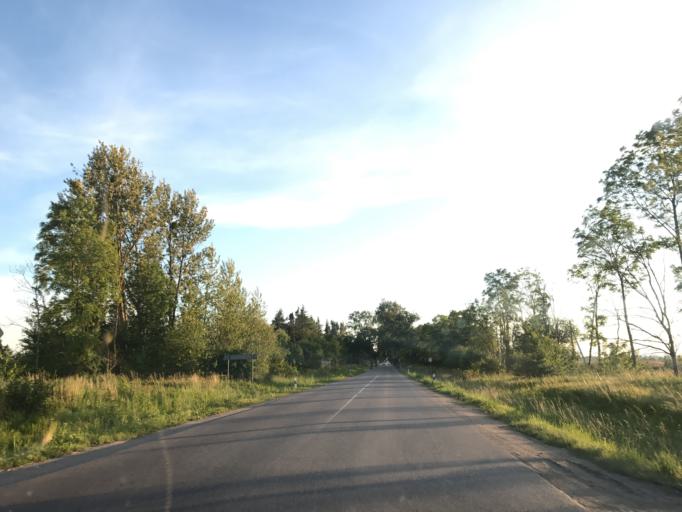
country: RU
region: Kaliningrad
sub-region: Zelenogradskiy Rayon
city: Zelenogradsk
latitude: 54.9380
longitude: 20.4486
